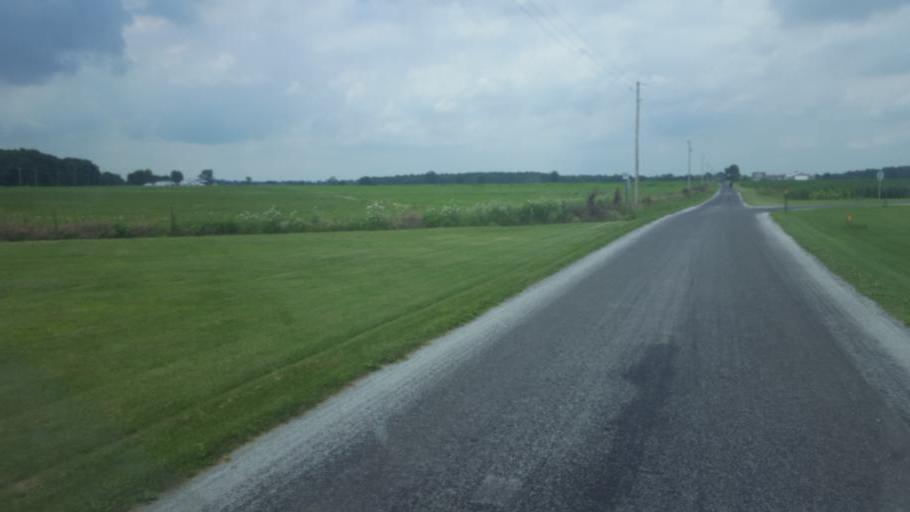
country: US
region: Ohio
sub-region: Hardin County
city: Kenton
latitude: 40.5838
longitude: -83.5194
